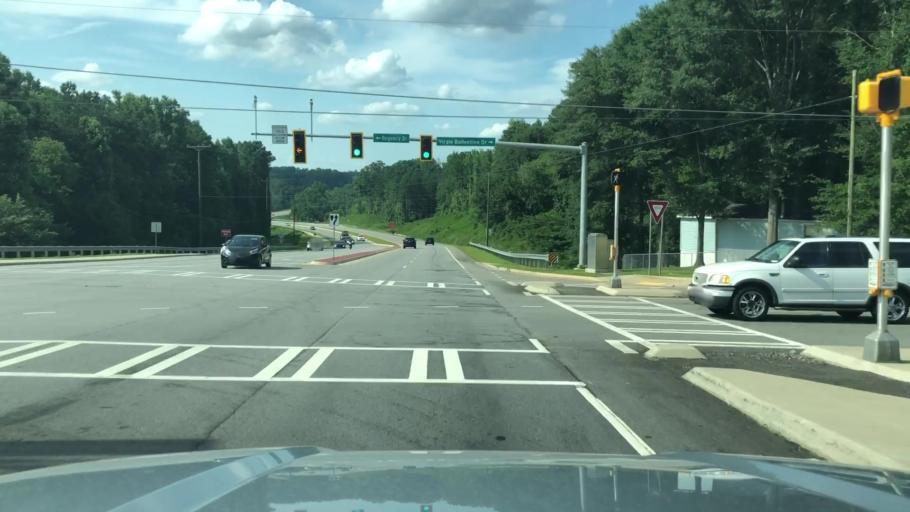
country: US
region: Georgia
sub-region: Paulding County
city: Hiram
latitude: 33.8732
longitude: -84.7811
